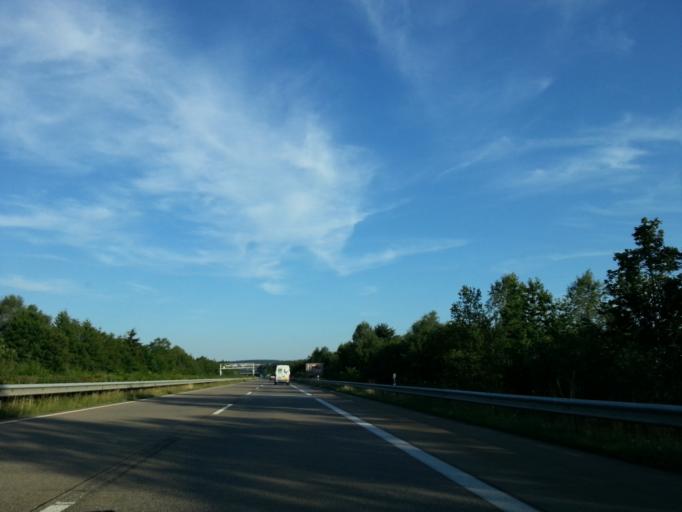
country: DE
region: Rheinland-Pfalz
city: Hinzert-Polert
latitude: 49.6831
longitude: 6.9068
